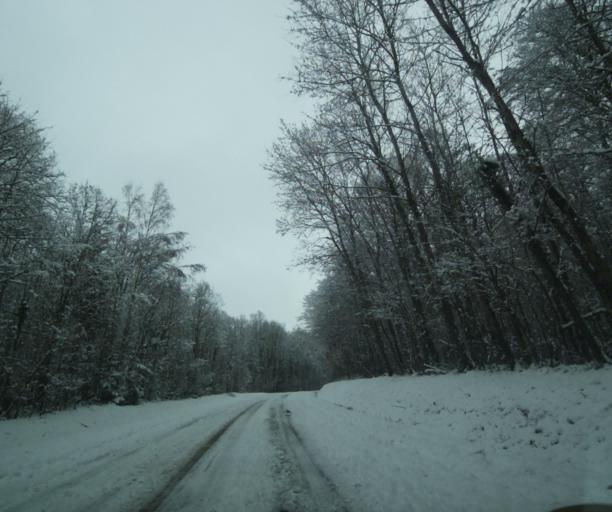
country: FR
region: Champagne-Ardenne
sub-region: Departement de la Haute-Marne
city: Montier-en-Der
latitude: 48.5415
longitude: 4.8056
